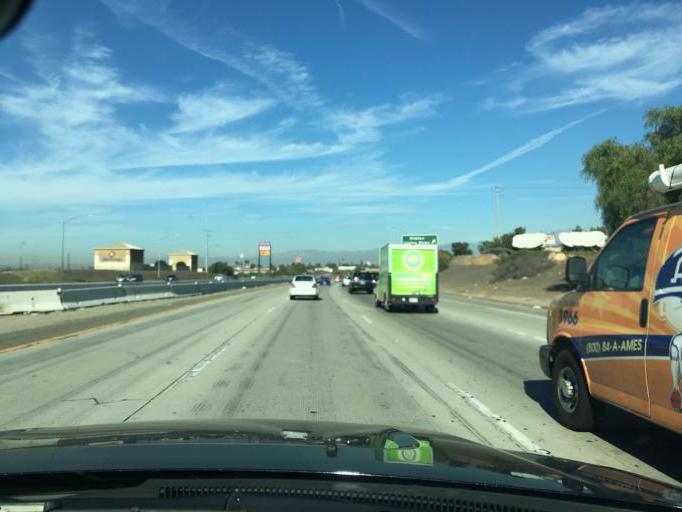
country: US
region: California
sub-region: Riverside County
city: Corona
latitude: 33.8937
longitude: -117.5570
